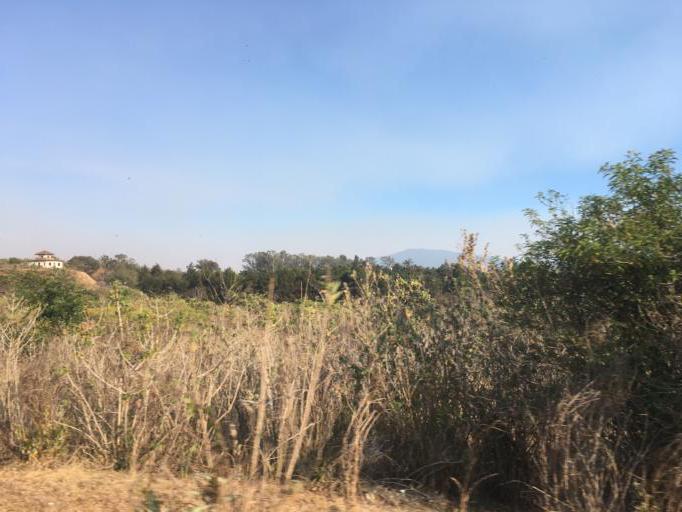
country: MX
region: Michoacan
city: Santa Fe de la Laguna
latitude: 19.6818
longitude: -101.5790
